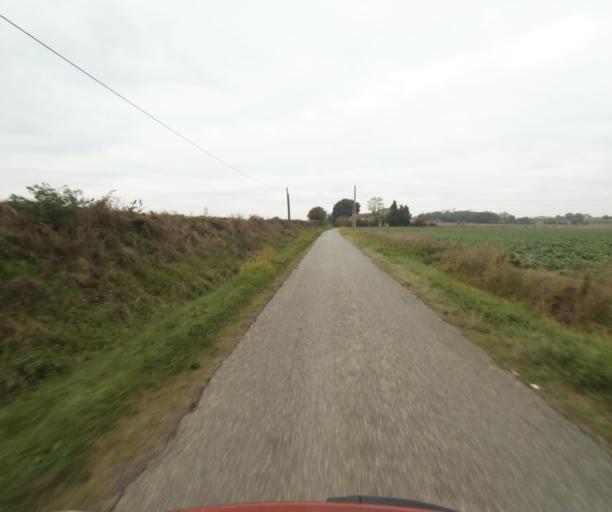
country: FR
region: Midi-Pyrenees
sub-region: Departement du Tarn-et-Garonne
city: Verdun-sur-Garonne
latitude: 43.8120
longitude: 1.2083
